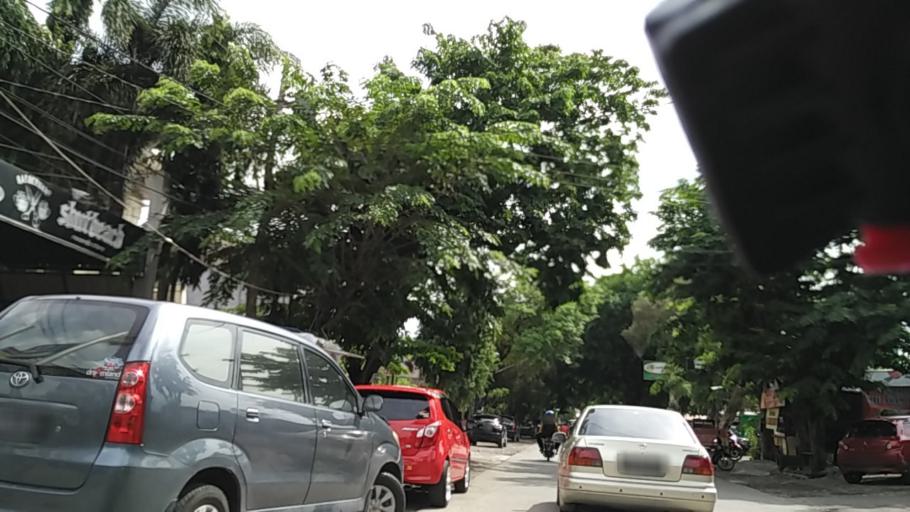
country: ID
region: Central Java
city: Semarang
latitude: -6.9962
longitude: 110.4252
